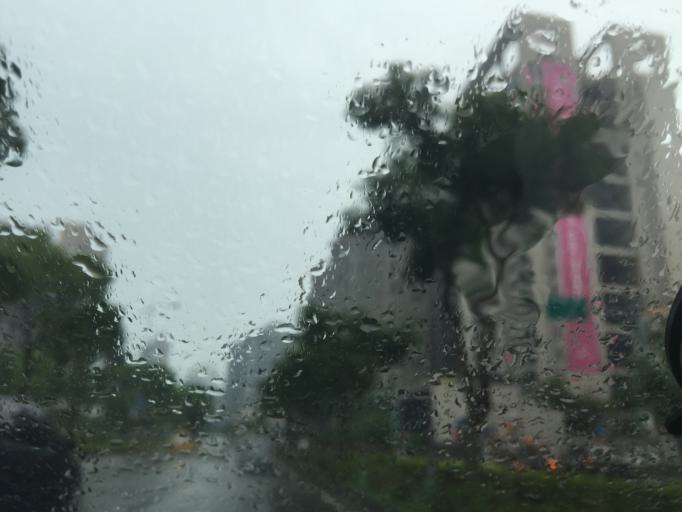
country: TW
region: Taiwan
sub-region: Hsinchu
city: Zhubei
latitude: 24.8148
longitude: 121.0326
